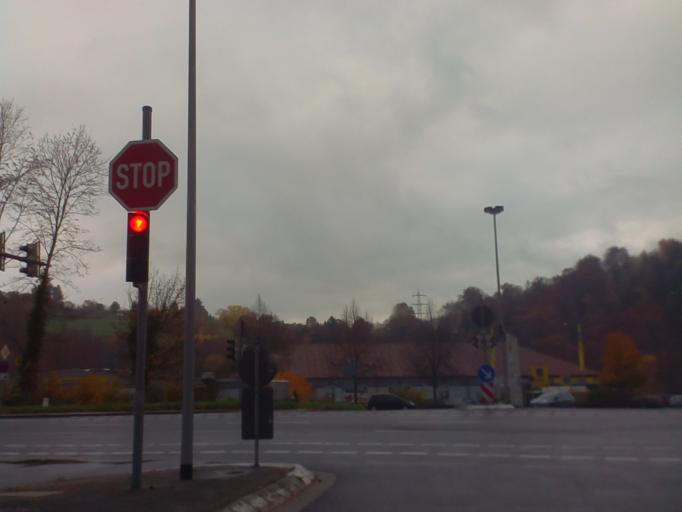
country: DE
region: Hesse
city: Neckarsteinach
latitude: 49.3983
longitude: 8.8509
